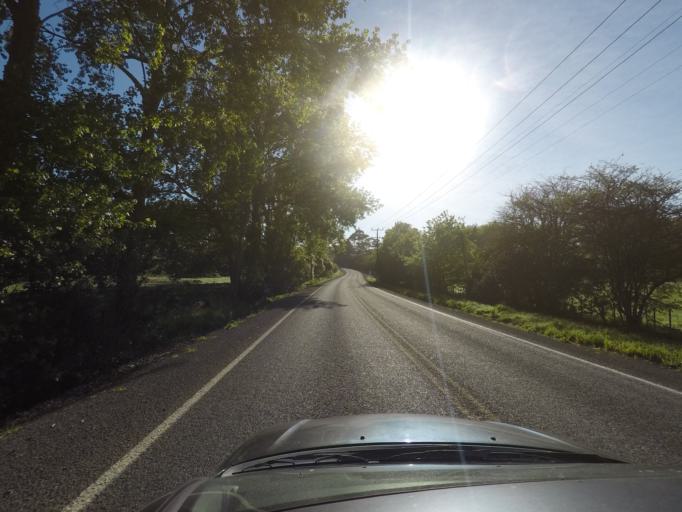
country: NZ
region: Auckland
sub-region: Auckland
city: Red Hill
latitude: -36.9965
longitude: 174.9802
